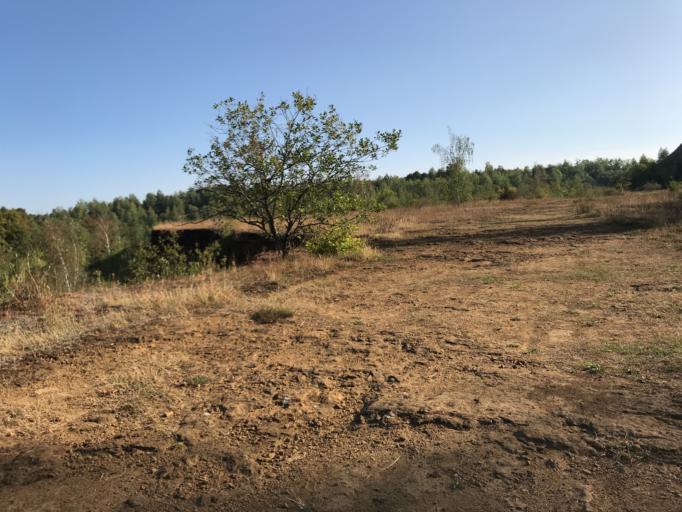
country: LU
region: Luxembourg
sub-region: Canton d'Esch-sur-Alzette
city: Niedercorn
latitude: 49.5405
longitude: 5.8764
